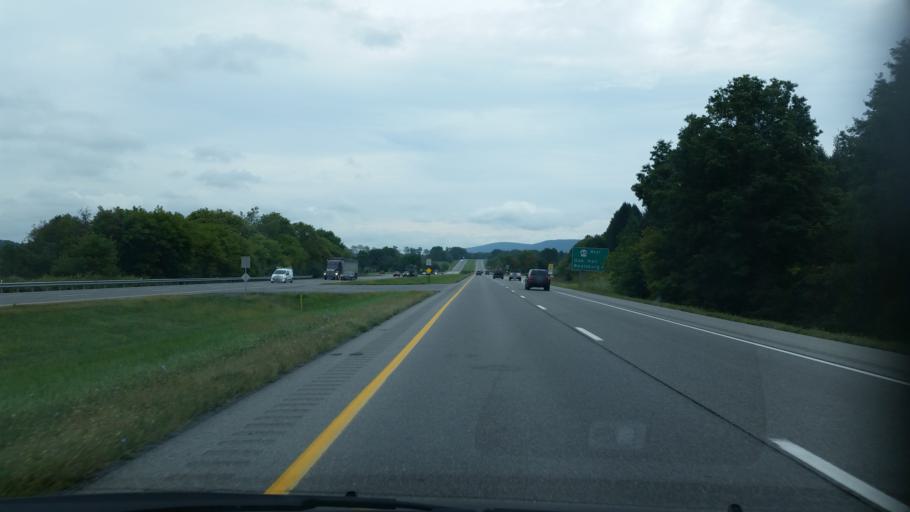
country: US
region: Pennsylvania
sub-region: Centre County
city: Boalsburg
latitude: 40.7906
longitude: -77.8078
